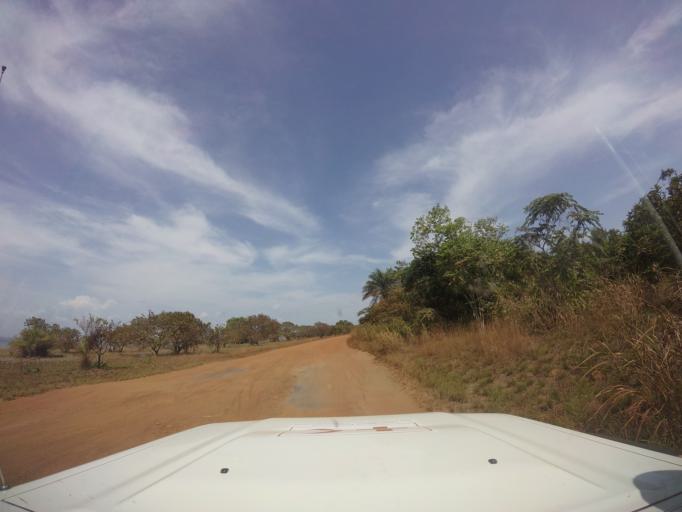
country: LR
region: Grand Cape Mount
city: Robertsport
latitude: 6.6874
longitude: -11.2507
